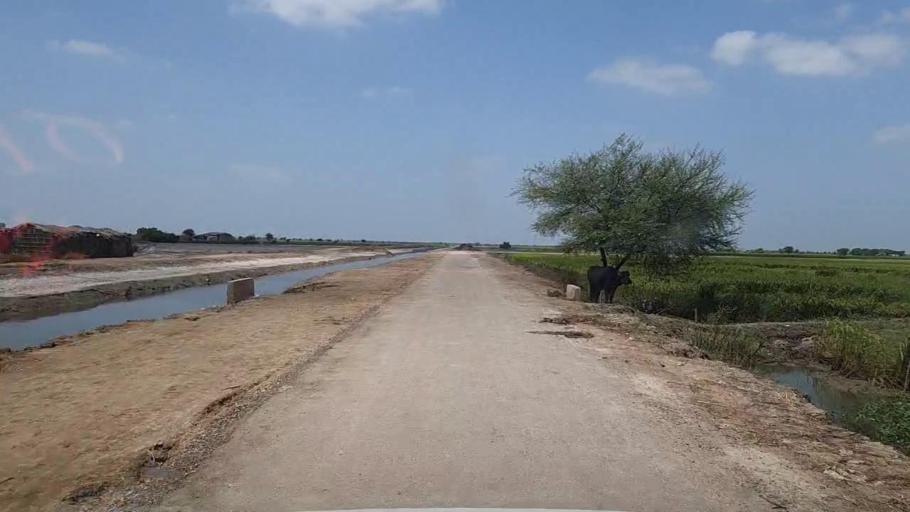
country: PK
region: Sindh
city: Kario
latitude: 24.6816
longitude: 68.5891
